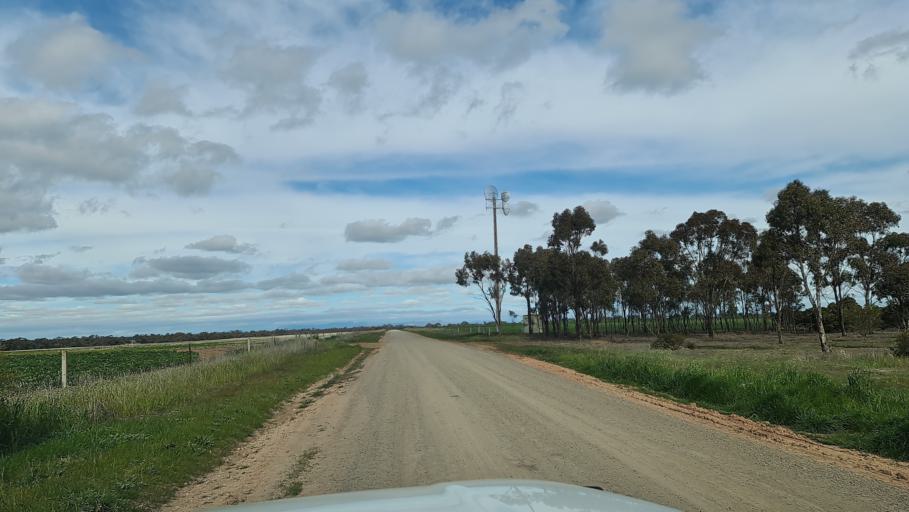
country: AU
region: Victoria
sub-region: Horsham
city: Horsham
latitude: -36.6204
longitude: 142.4118
